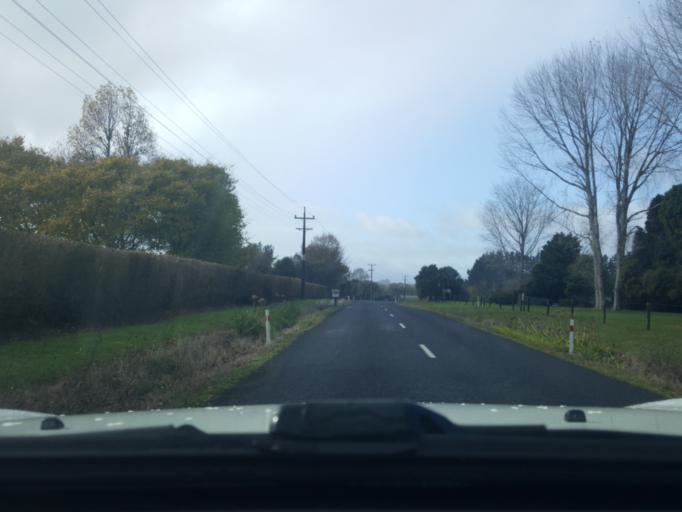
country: NZ
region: Auckland
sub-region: Auckland
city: Pukekohe East
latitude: -37.3510
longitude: 174.9885
